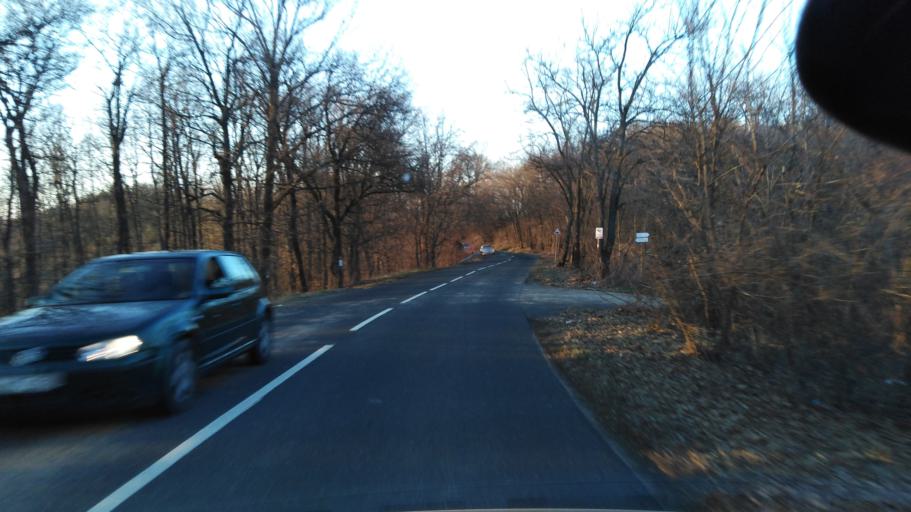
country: HU
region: Nograd
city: Salgotarjan
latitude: 48.0741
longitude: 19.8131
